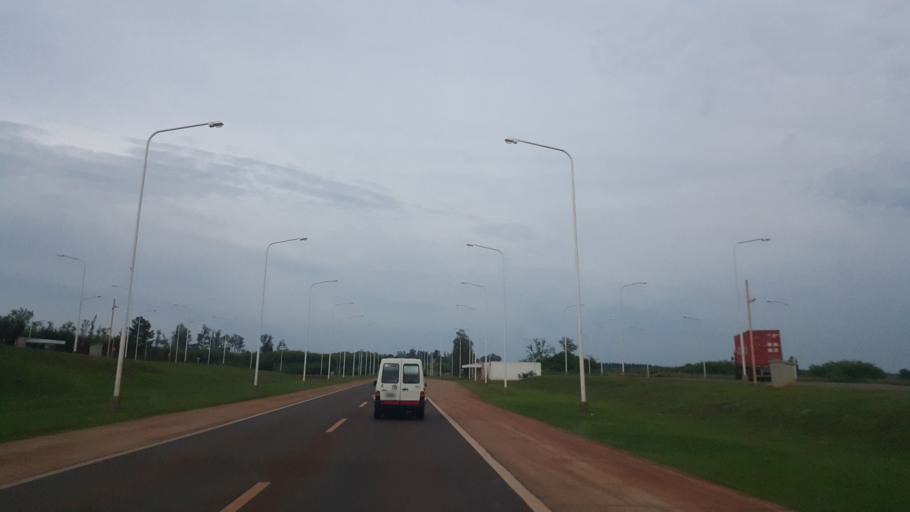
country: AR
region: Misiones
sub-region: Departamento de Apostoles
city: San Jose
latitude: -27.7823
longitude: -55.8183
